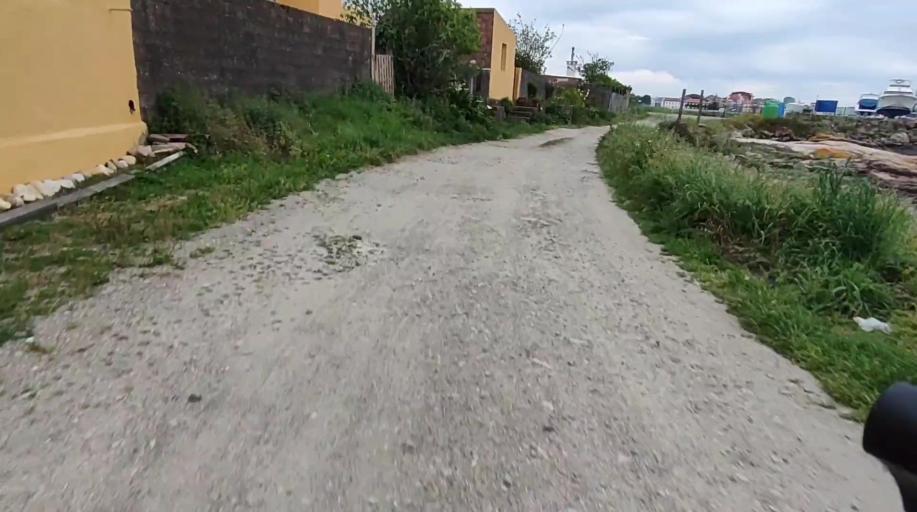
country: ES
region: Galicia
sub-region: Provincia da Coruna
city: Boiro
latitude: 42.6194
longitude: -8.8868
